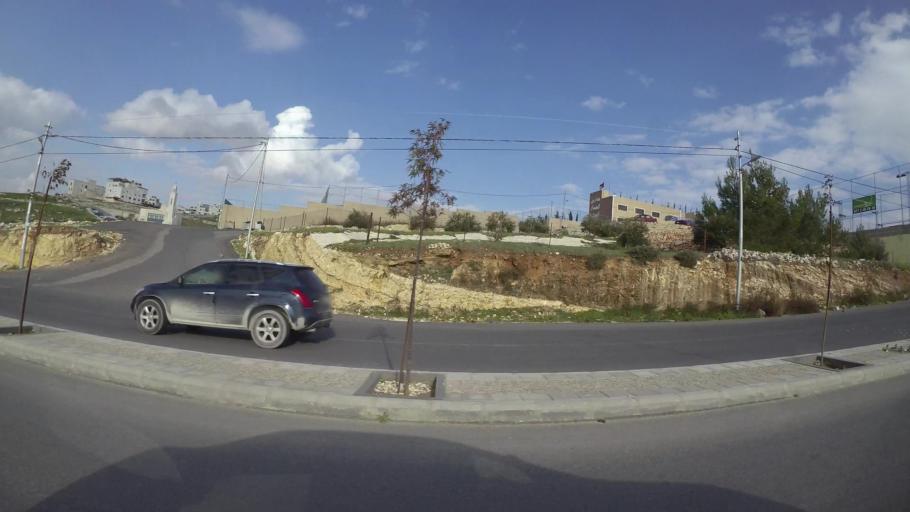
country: JO
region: Amman
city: Wadi as Sir
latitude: 31.9301
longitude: 35.8482
